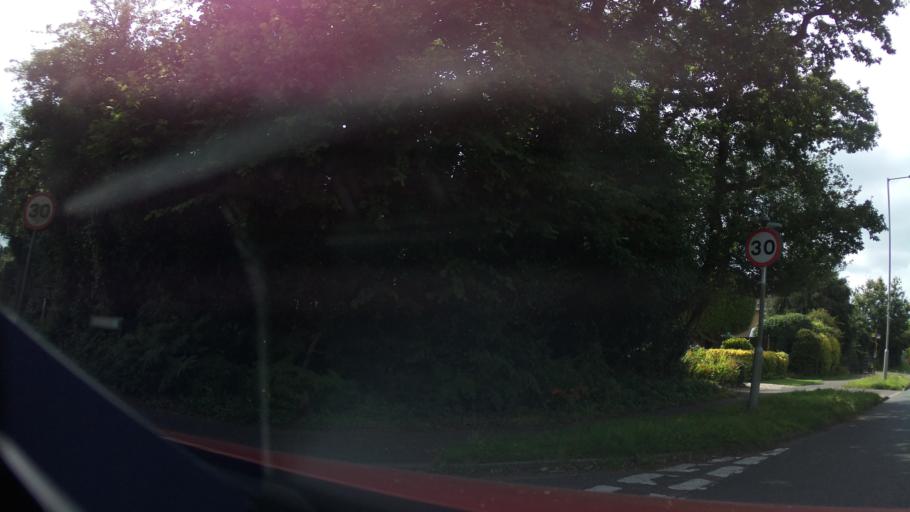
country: GB
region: England
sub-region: Hampshire
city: New Milton
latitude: 50.7482
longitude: -1.6915
